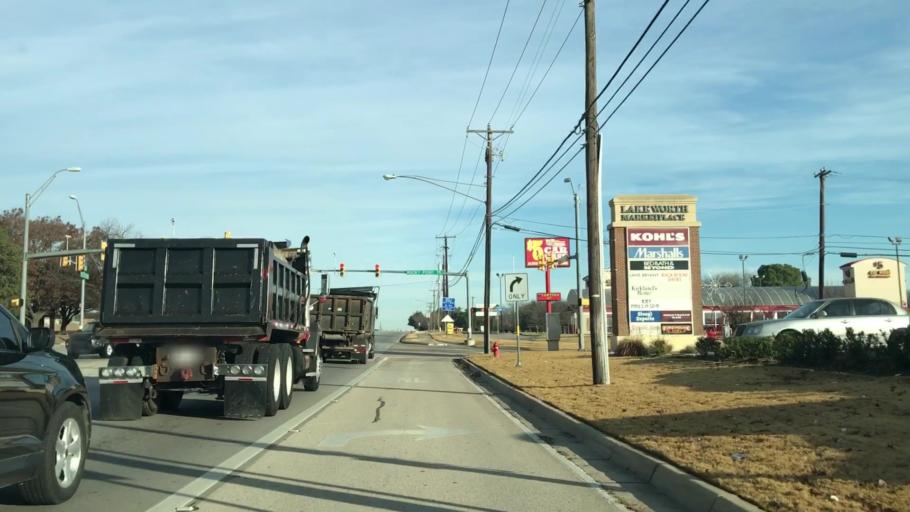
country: US
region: Texas
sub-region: Tarrant County
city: Sansom Park
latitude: 32.8171
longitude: -97.4199
